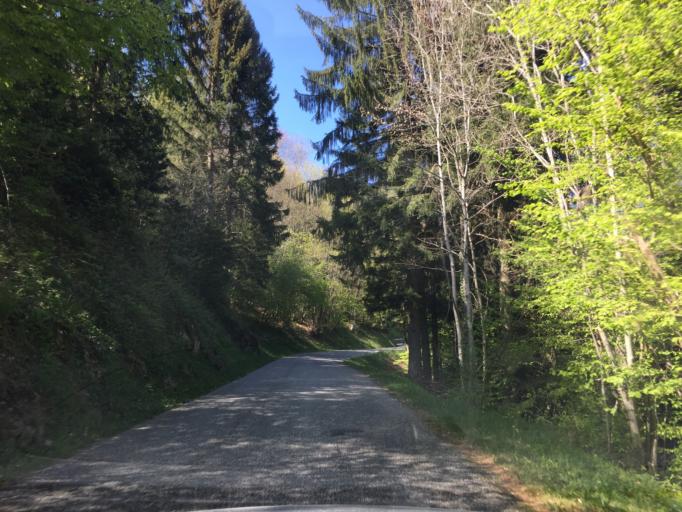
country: FR
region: Rhone-Alpes
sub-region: Departement de la Savoie
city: Vimines
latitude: 45.5780
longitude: 5.8314
